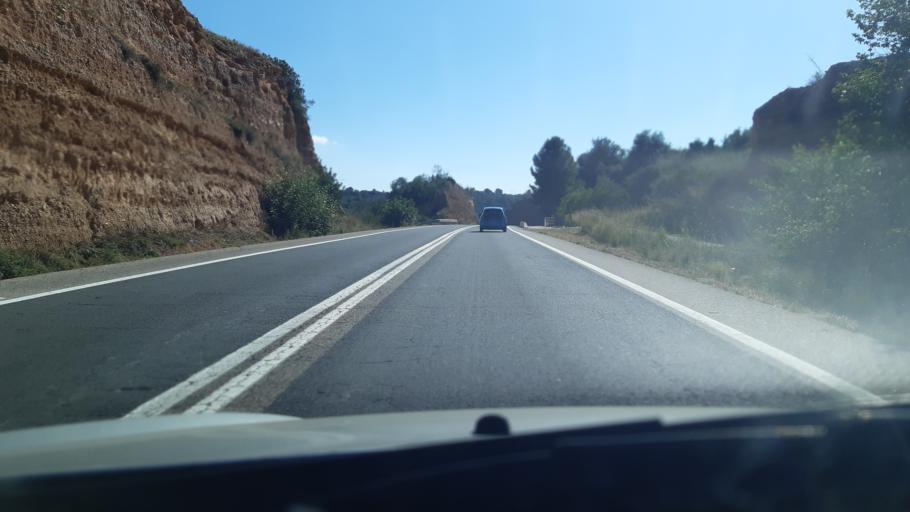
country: ES
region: Catalonia
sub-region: Provincia de Tarragona
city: Tivenys
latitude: 40.8880
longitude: 0.4913
